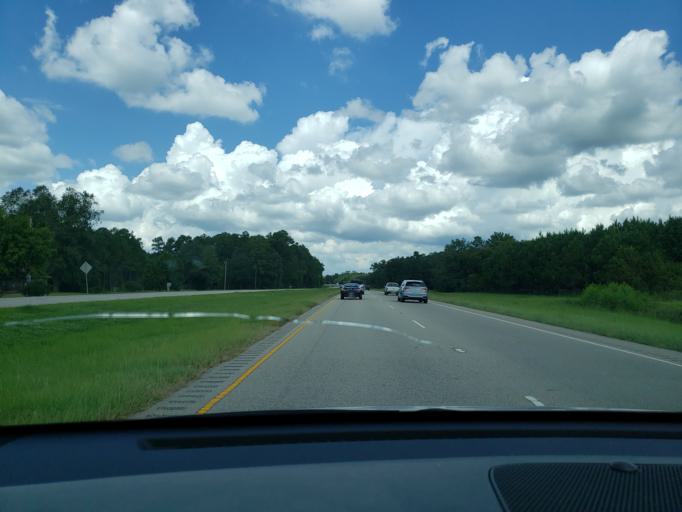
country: US
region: North Carolina
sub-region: Bladen County
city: Elizabethtown
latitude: 34.6952
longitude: -78.7401
